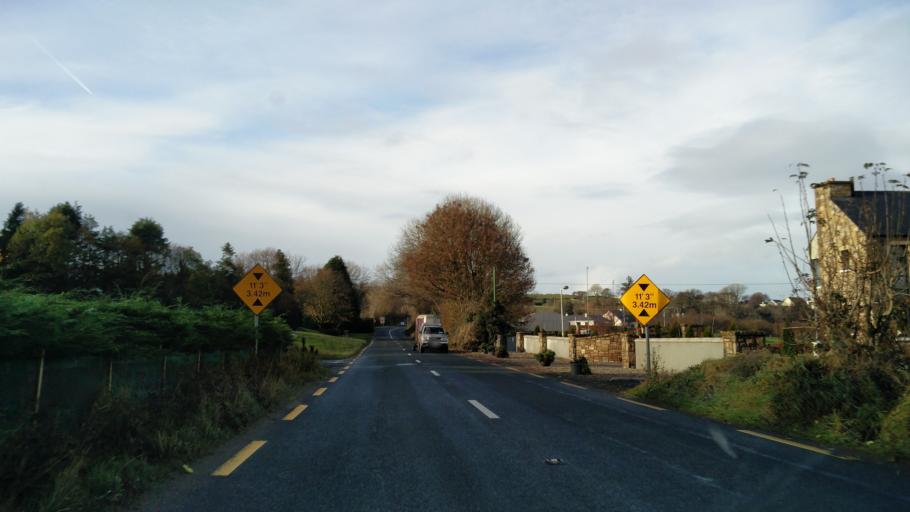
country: IE
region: Connaught
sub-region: Maigh Eo
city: Westport
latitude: 53.7884
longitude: -9.4995
